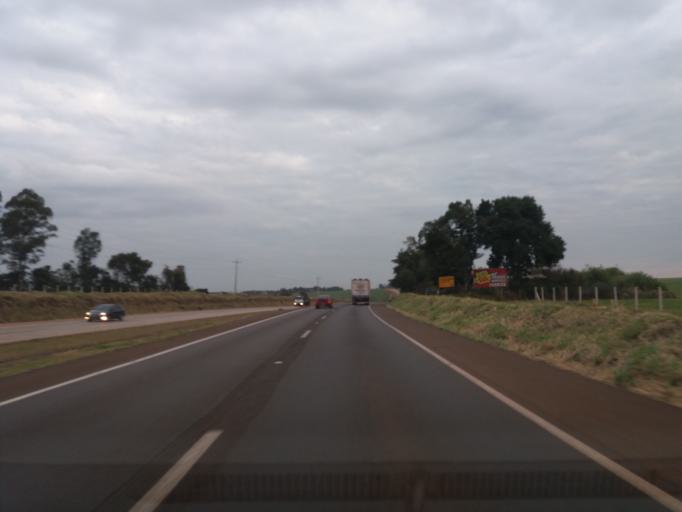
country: BR
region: Parana
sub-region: Cascavel
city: Cascavel
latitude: -25.1200
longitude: -53.5857
